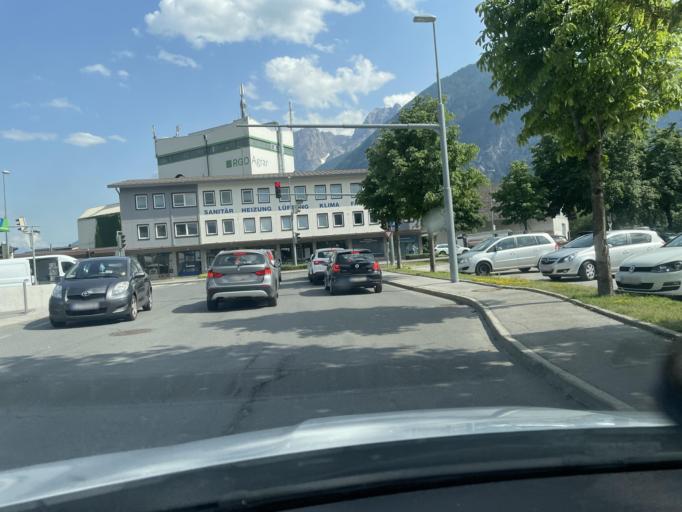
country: AT
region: Tyrol
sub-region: Politischer Bezirk Lienz
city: Lienz
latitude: 46.8310
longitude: 12.7749
